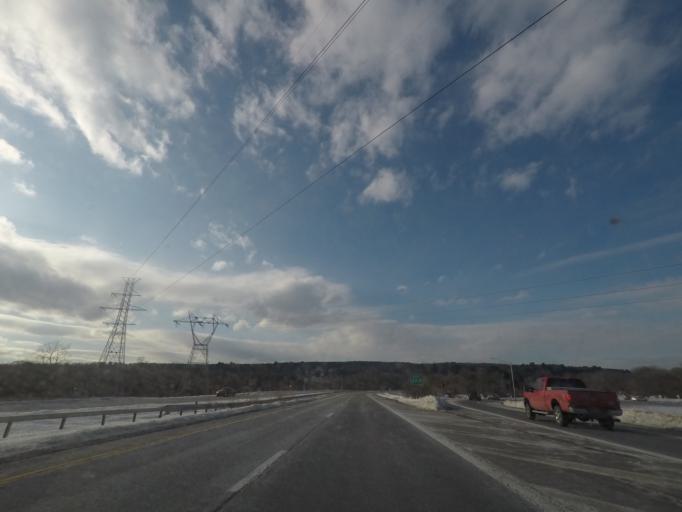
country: US
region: New York
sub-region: Schenectady County
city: Scotia
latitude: 42.8150
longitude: -73.9816
